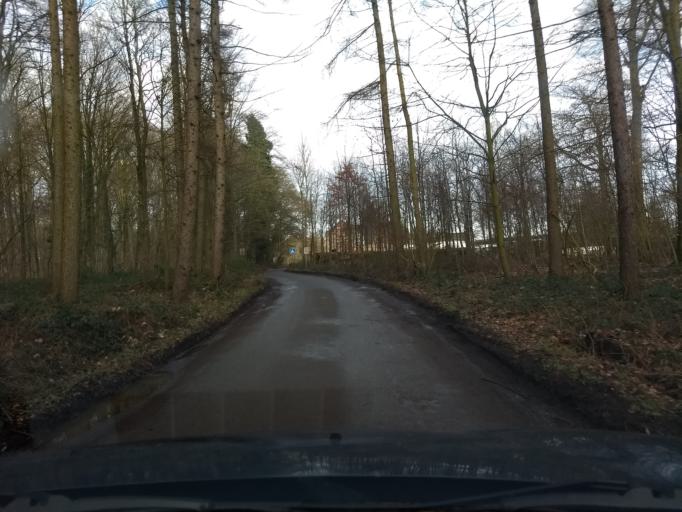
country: BE
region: Wallonia
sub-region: Province du Brabant Wallon
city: Braine-le-Chateau
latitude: 50.6900
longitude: 4.2482
